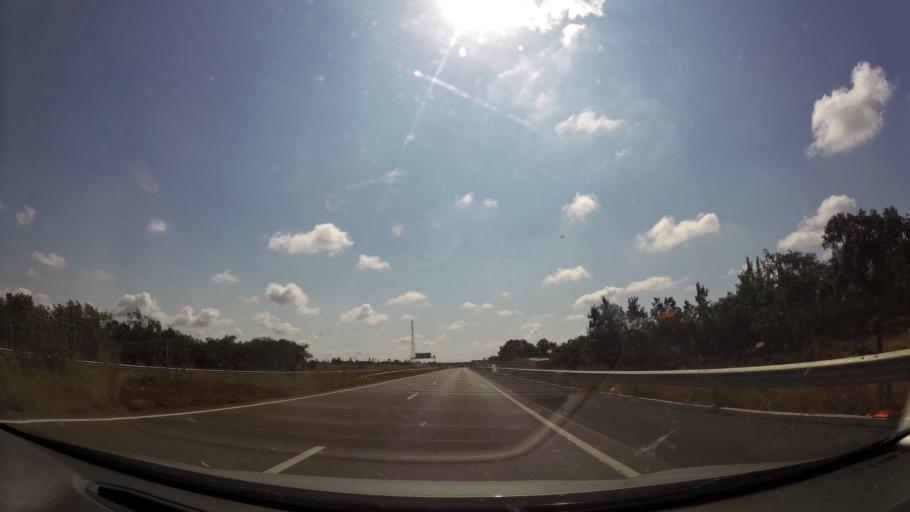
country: MA
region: Rabat-Sale-Zemmour-Zaer
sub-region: Skhirate-Temara
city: Temara
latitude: 33.8406
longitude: -6.8576
